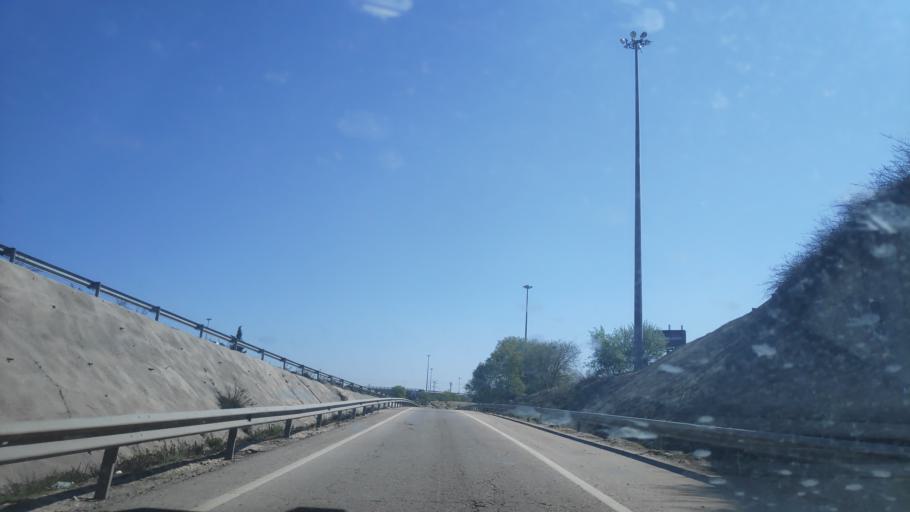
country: ES
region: Madrid
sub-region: Provincia de Madrid
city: Pinto
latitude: 40.2739
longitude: -3.6964
